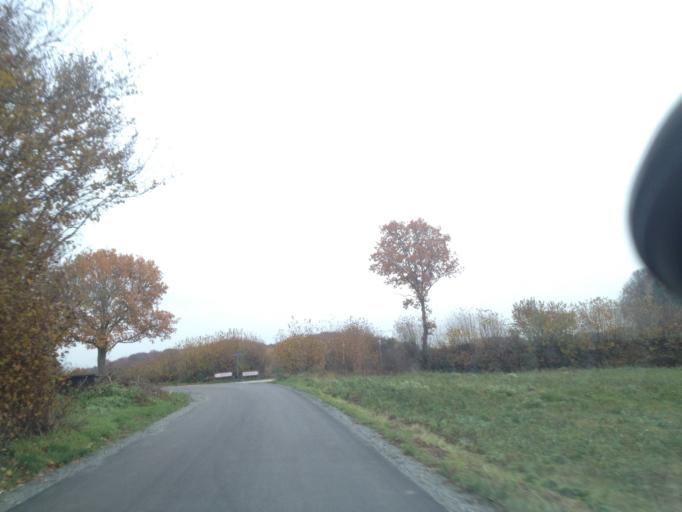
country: DK
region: South Denmark
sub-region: Nordfyns Kommune
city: Sonderso
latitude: 55.4253
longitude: 10.2276
